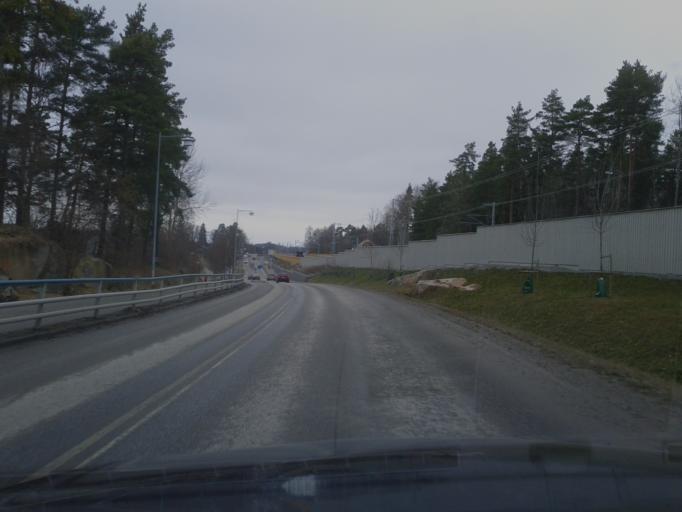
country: SE
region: Stockholm
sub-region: Vallentuna Kommun
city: Vallentuna
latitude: 59.5201
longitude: 18.0731
